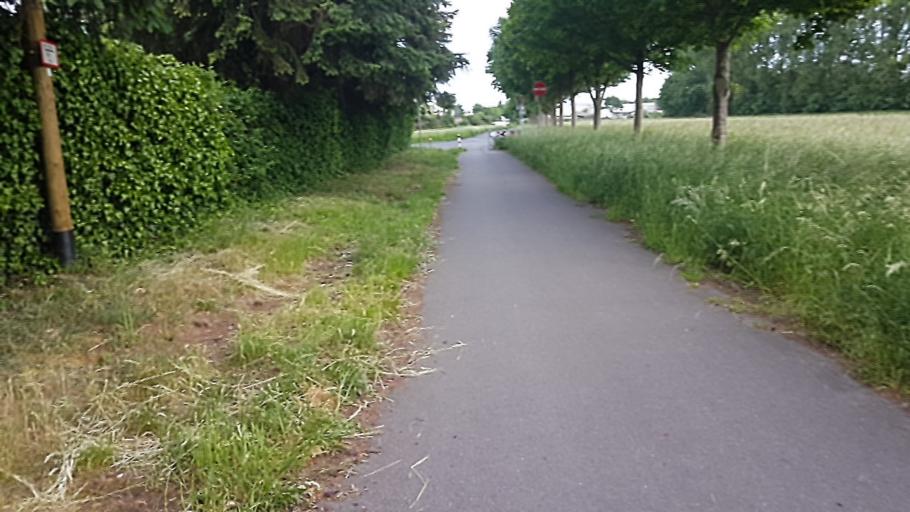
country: DE
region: North Rhine-Westphalia
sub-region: Regierungsbezirk Dusseldorf
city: Hochfeld
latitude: 51.3596
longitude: 6.7731
